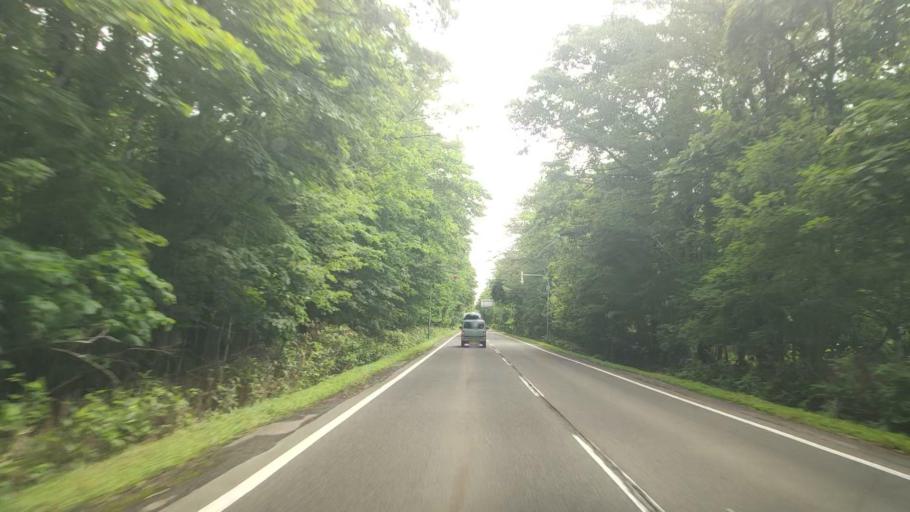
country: JP
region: Hokkaido
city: Chitose
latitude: 42.7803
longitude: 141.4409
